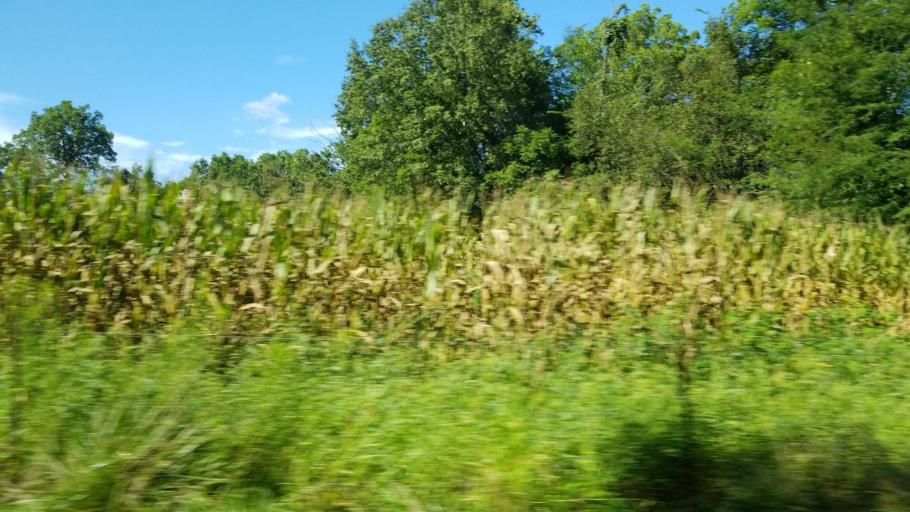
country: US
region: Illinois
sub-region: Williamson County
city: Johnston City
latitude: 37.7845
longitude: -88.8112
